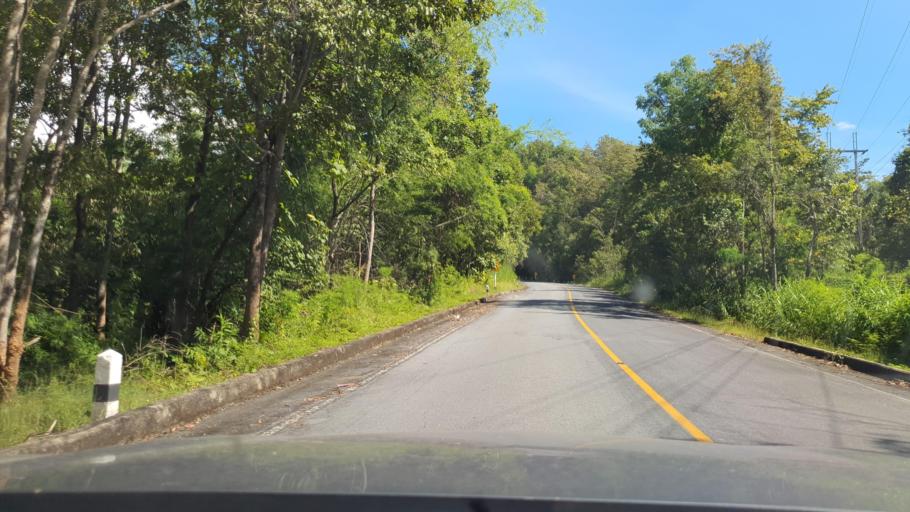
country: TH
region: Chiang Mai
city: Phrao
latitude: 19.3595
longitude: 99.2671
